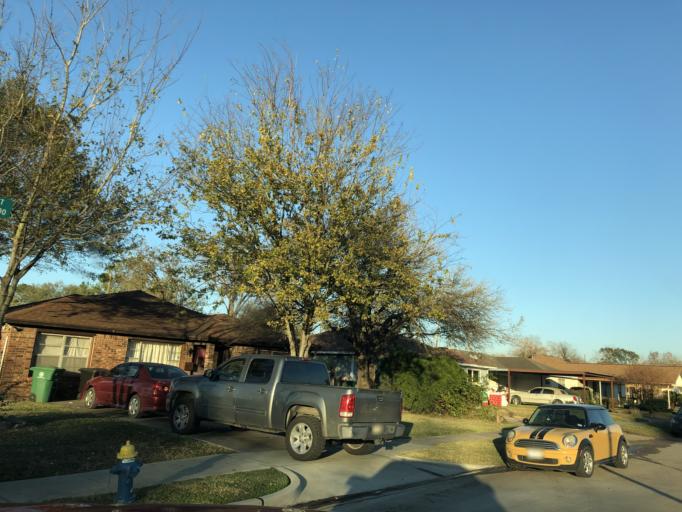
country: US
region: Texas
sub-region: Harris County
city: Jacinto City
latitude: 29.7610
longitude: -95.2724
